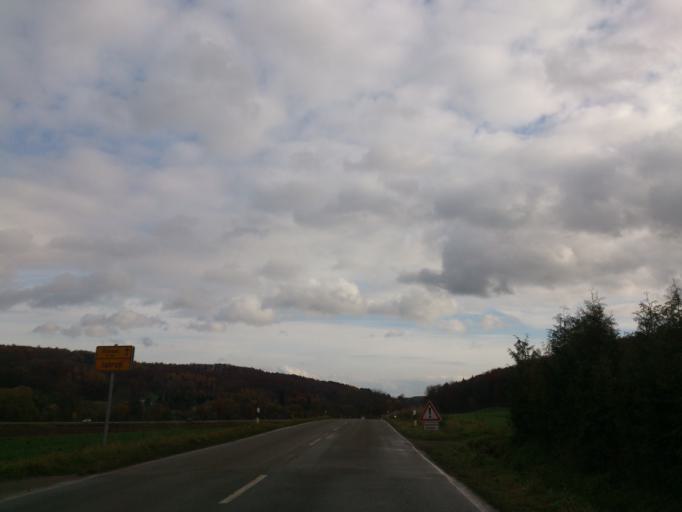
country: DE
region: North Rhine-Westphalia
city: Brakel
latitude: 51.7074
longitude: 9.1240
